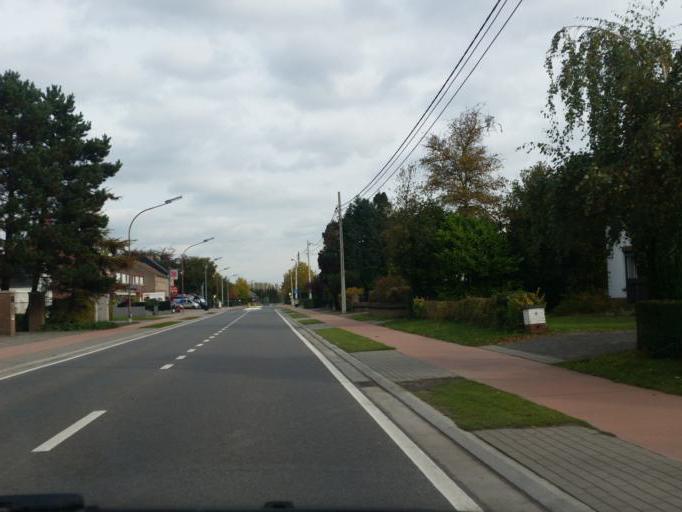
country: BE
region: Flanders
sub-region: Provincie Antwerpen
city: Sint-Katelijne-Waver
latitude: 51.0452
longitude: 4.5223
